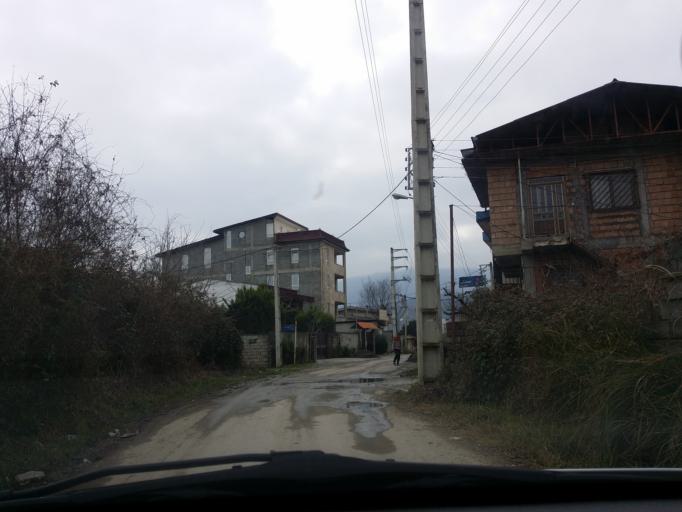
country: IR
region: Mazandaran
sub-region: Nowshahr
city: Nowshahr
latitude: 36.6458
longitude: 51.4747
